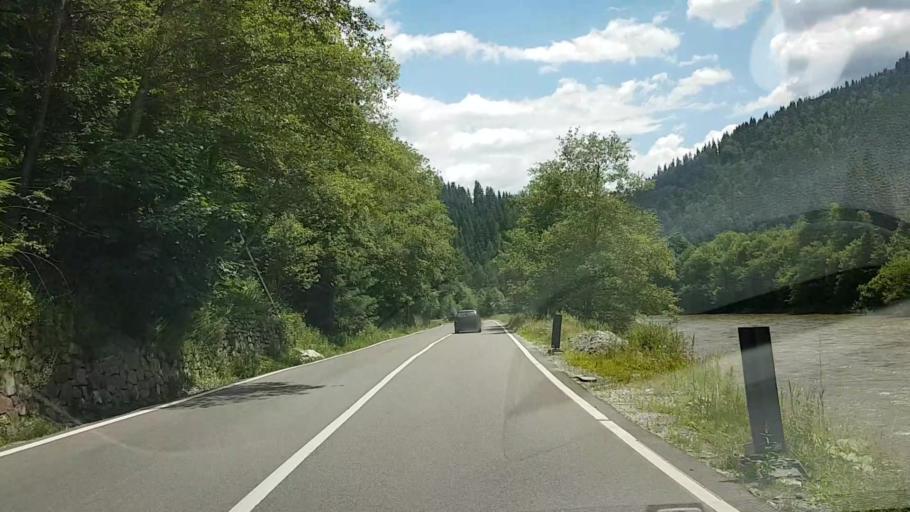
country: RO
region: Suceava
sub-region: Comuna Brosteni
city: Brosteni
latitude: 47.2637
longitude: 25.6648
